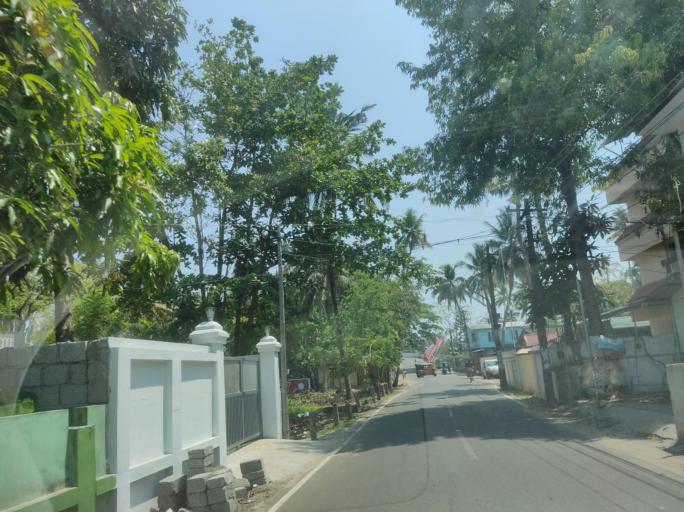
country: IN
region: Kerala
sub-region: Alappuzha
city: Arukutti
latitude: 9.8524
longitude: 76.2939
